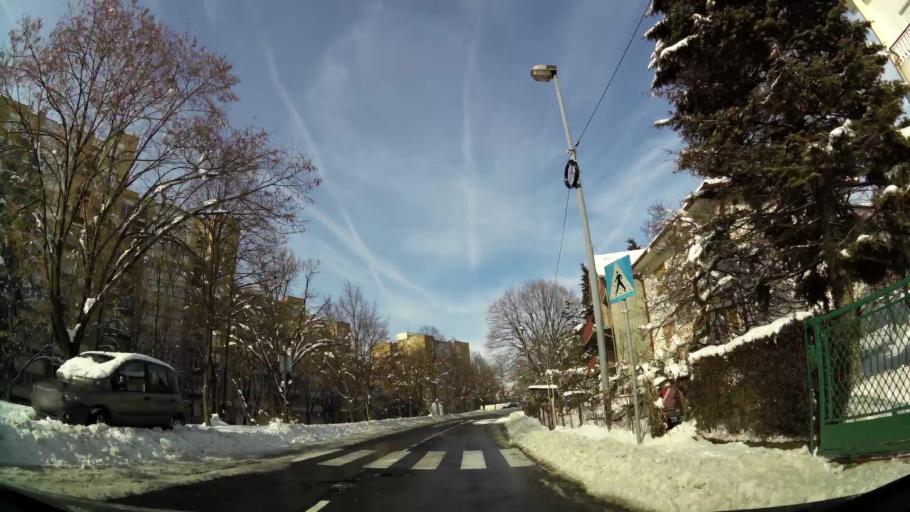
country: RS
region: Central Serbia
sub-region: Belgrade
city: Zvezdara
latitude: 44.7916
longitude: 20.5353
